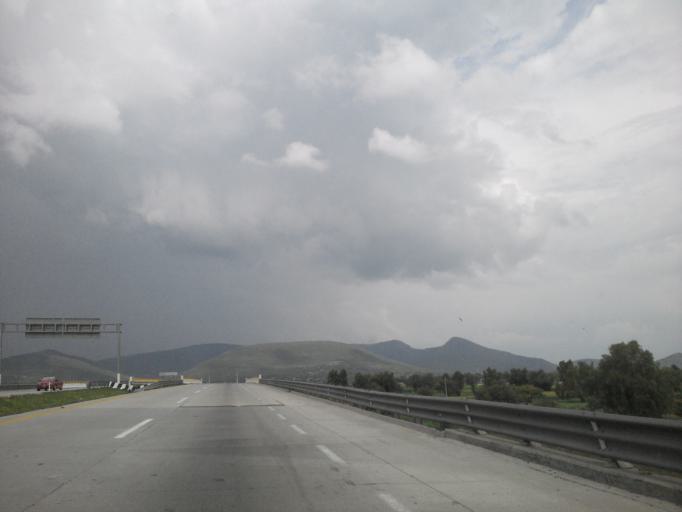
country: MX
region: Hidalgo
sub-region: Atitalaquia
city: Tezoquipa
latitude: 20.0642
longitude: -99.2116
